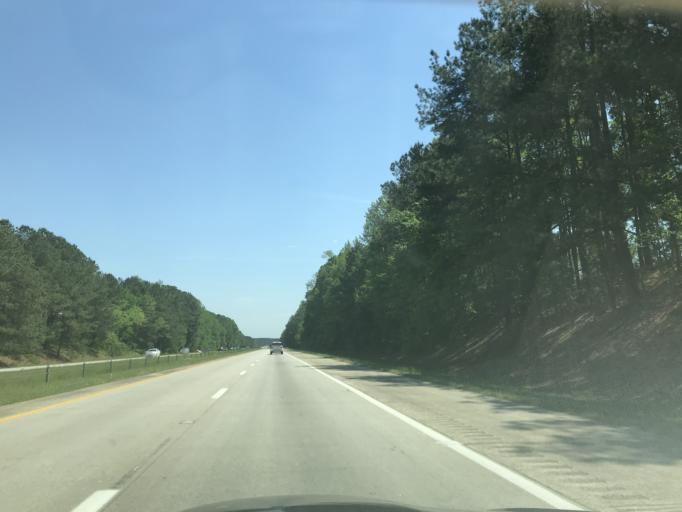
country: US
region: North Carolina
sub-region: Johnston County
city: Benson
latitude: 35.5309
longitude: -78.5684
